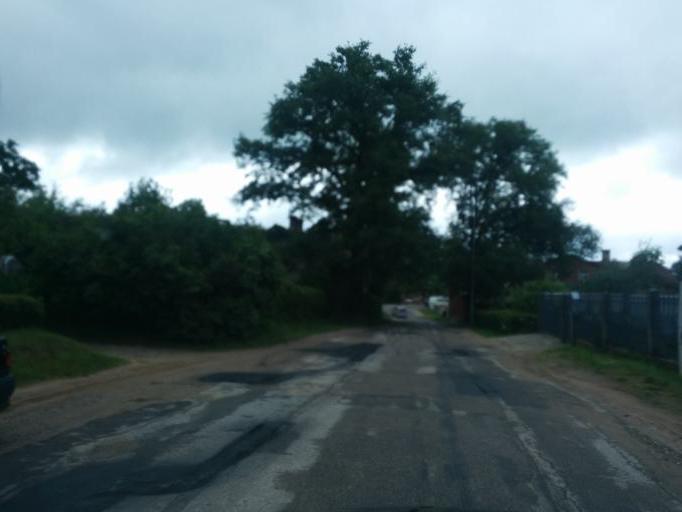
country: LV
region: Smiltene
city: Smiltene
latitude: 57.4267
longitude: 25.8947
